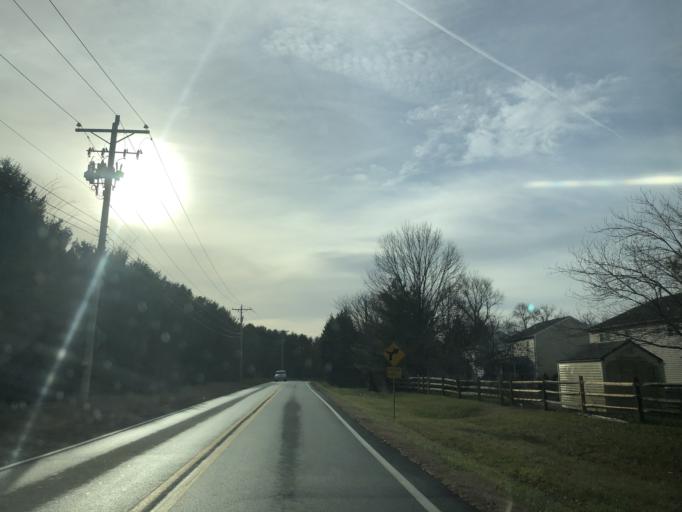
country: US
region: Delaware
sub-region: New Castle County
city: Townsend
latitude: 39.4421
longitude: -75.6444
